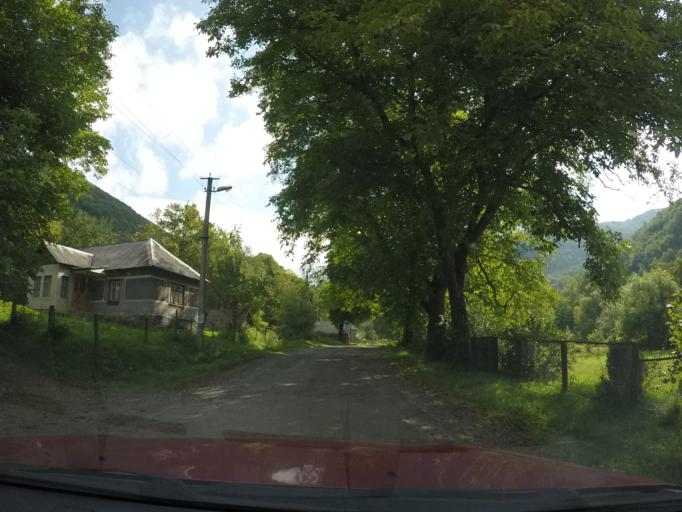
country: UA
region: Zakarpattia
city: Velykyi Bereznyi
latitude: 48.9432
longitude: 22.6321
